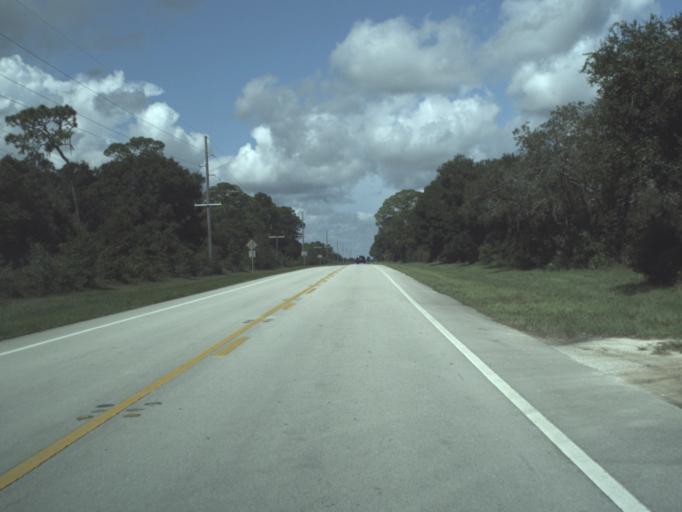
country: US
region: Florida
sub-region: Okeechobee County
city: Okeechobee
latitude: 27.3627
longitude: -81.0580
